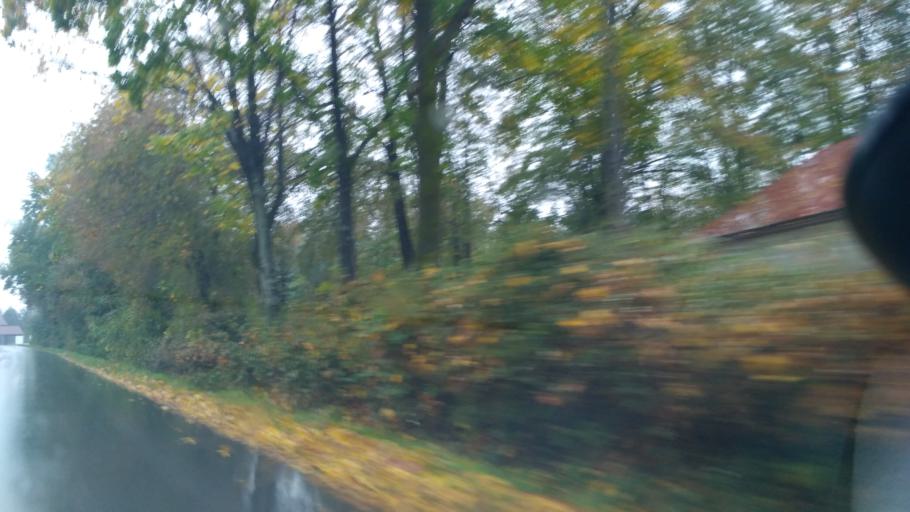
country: PL
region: Subcarpathian Voivodeship
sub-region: Powiat krosnienski
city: Kroscienko Wyzne
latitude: 49.6739
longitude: 21.8044
